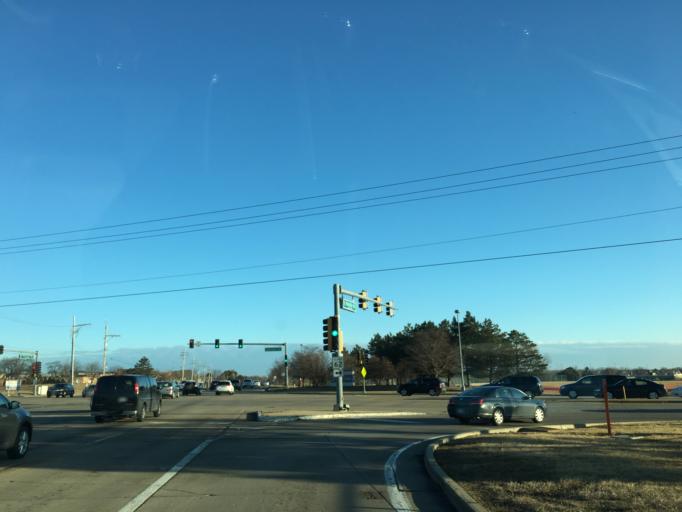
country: US
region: Illinois
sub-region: Cook County
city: Hoffman Estates
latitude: 42.0783
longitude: -88.0778
